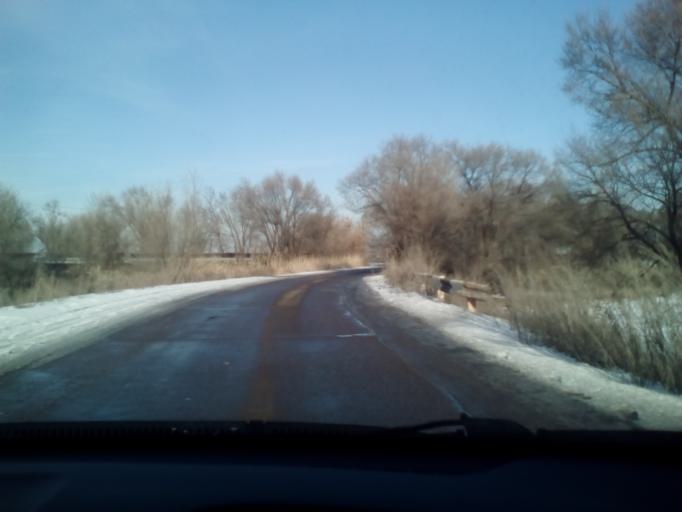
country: KZ
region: Almaty Oblysy
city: Burunday
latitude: 43.2220
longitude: 76.4105
